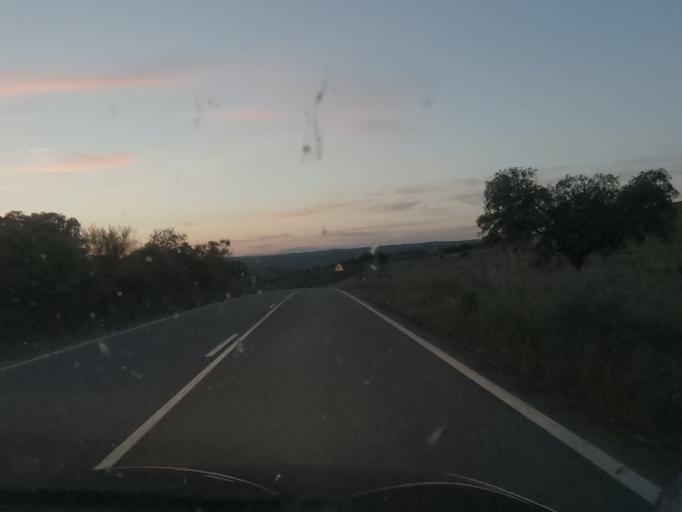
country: ES
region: Extremadura
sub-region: Provincia de Caceres
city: Piedras Albas
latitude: 39.7957
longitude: -6.9624
